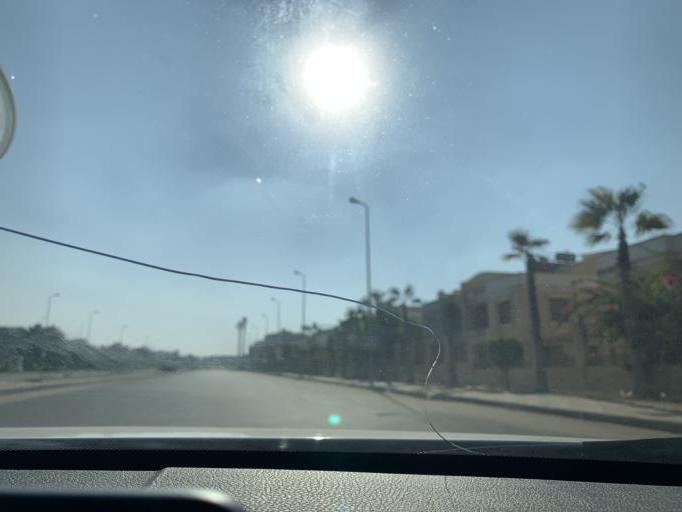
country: EG
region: Muhafazat al Qalyubiyah
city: Al Khankah
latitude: 30.0089
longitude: 31.4836
